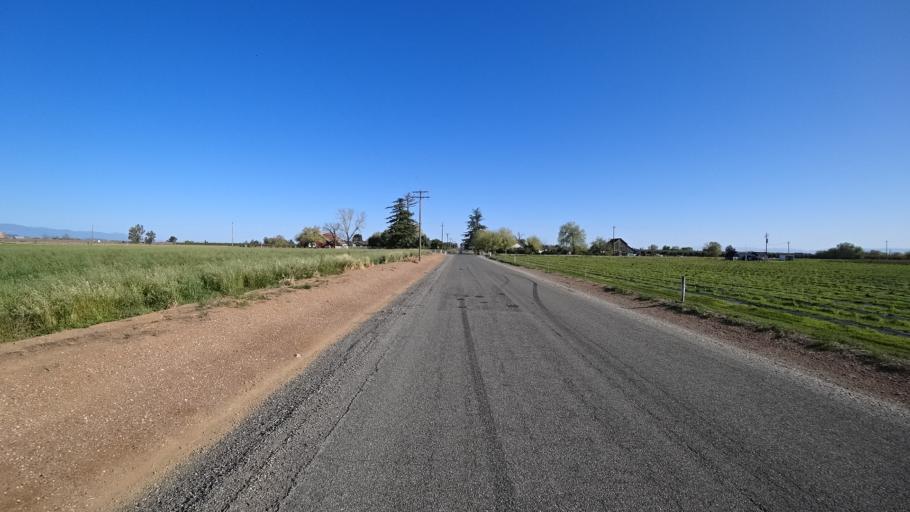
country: US
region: California
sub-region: Glenn County
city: Orland
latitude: 39.7430
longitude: -122.2390
